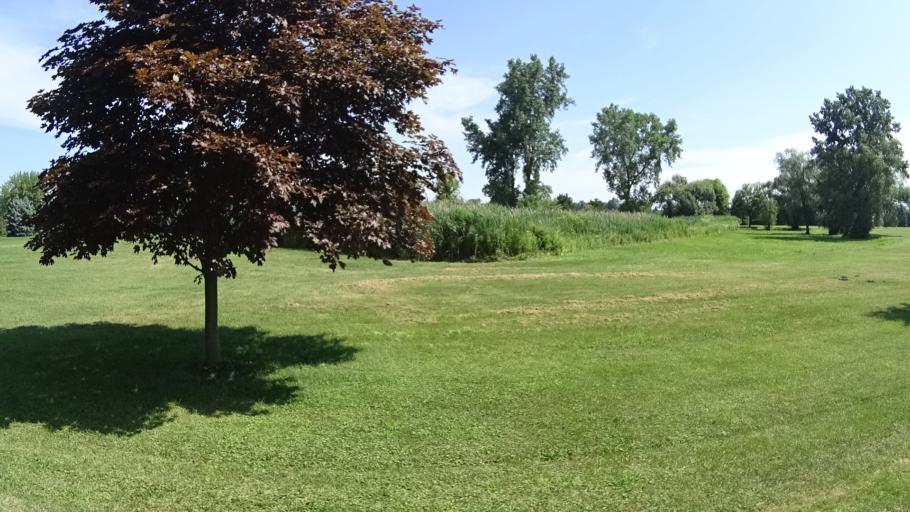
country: US
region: Ohio
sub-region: Erie County
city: Sandusky
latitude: 41.4210
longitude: -82.8090
